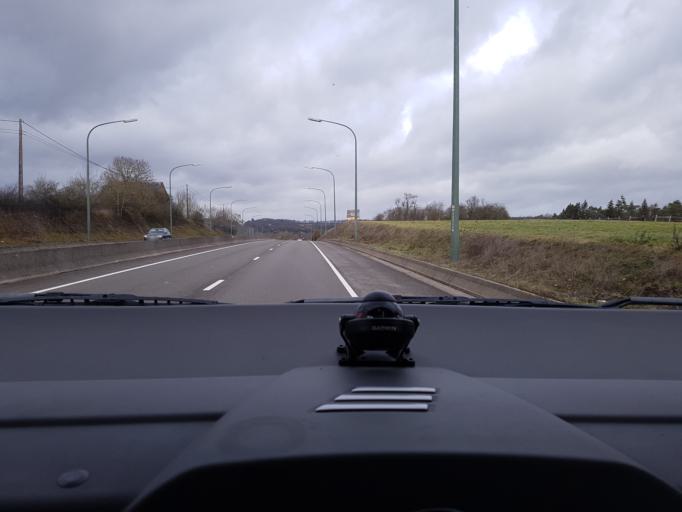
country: BE
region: Wallonia
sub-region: Province du Luxembourg
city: Marche-en-Famenne
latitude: 50.2434
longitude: 5.2889
